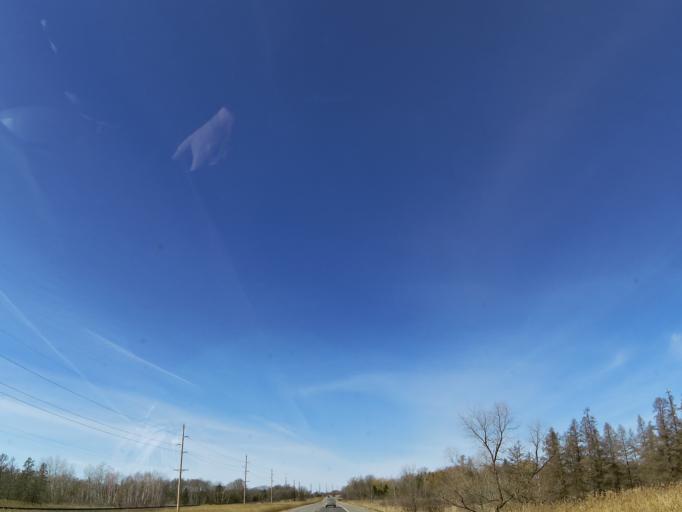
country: US
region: Minnesota
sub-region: Wright County
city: Annandale
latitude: 45.2666
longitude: -94.1432
